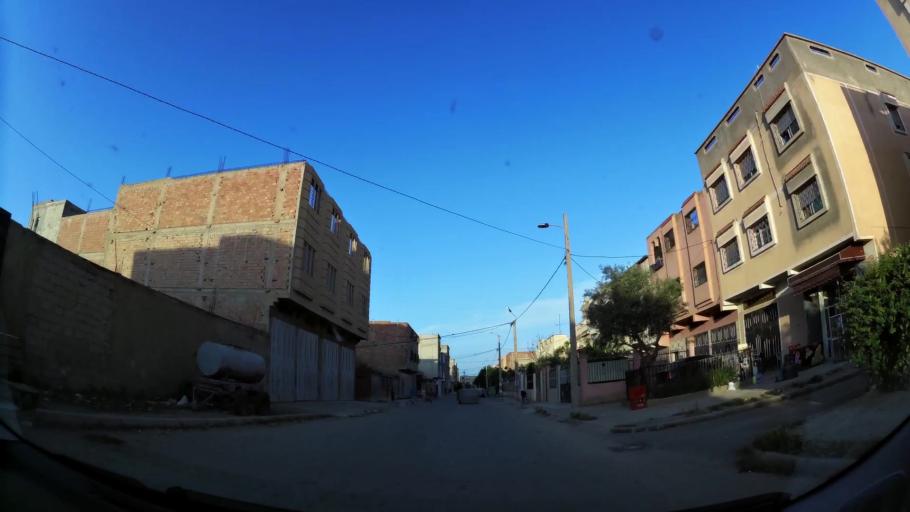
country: MA
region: Oriental
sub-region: Oujda-Angad
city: Oujda
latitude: 34.7094
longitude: -1.9132
